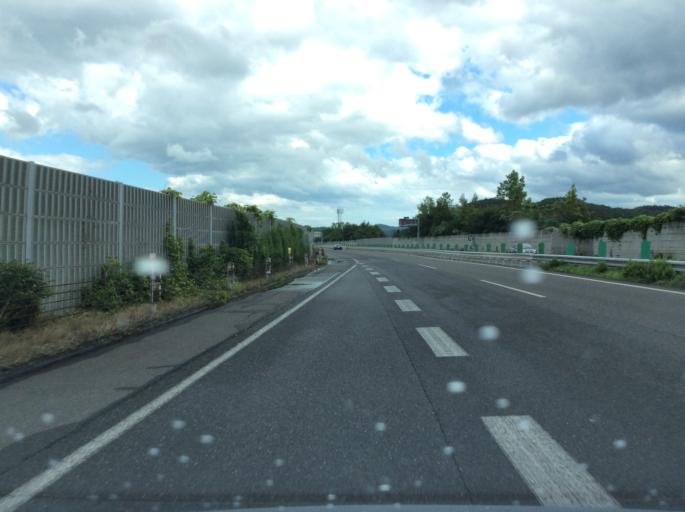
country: JP
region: Fukushima
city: Fukushima-shi
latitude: 37.7337
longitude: 140.4224
